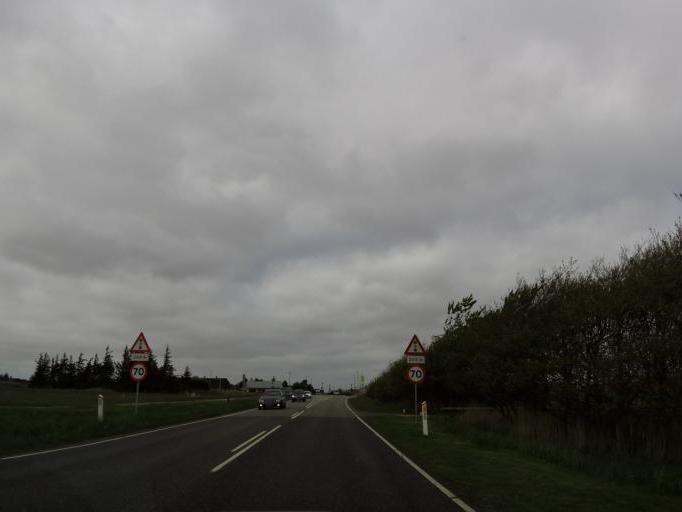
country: DE
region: Schleswig-Holstein
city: List
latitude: 55.1500
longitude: 8.5487
